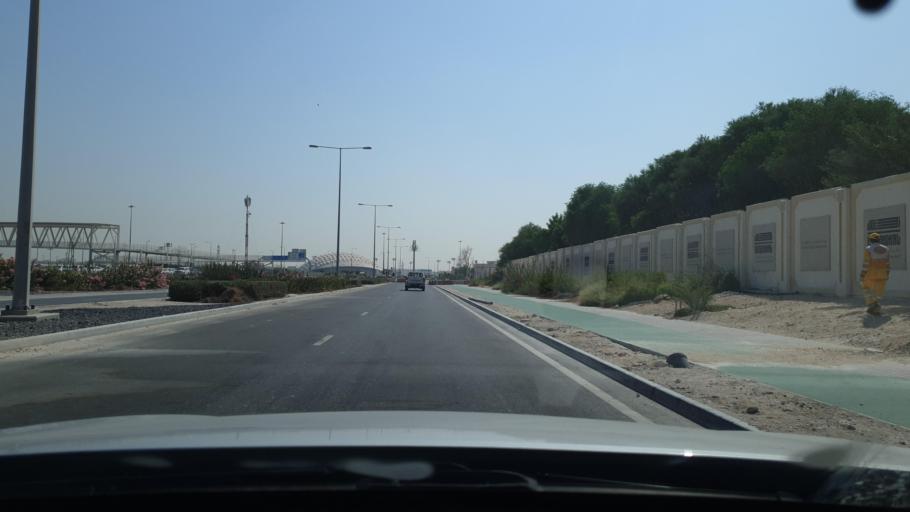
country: QA
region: Baladiyat ad Dawhah
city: Doha
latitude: 25.2308
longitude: 51.5275
